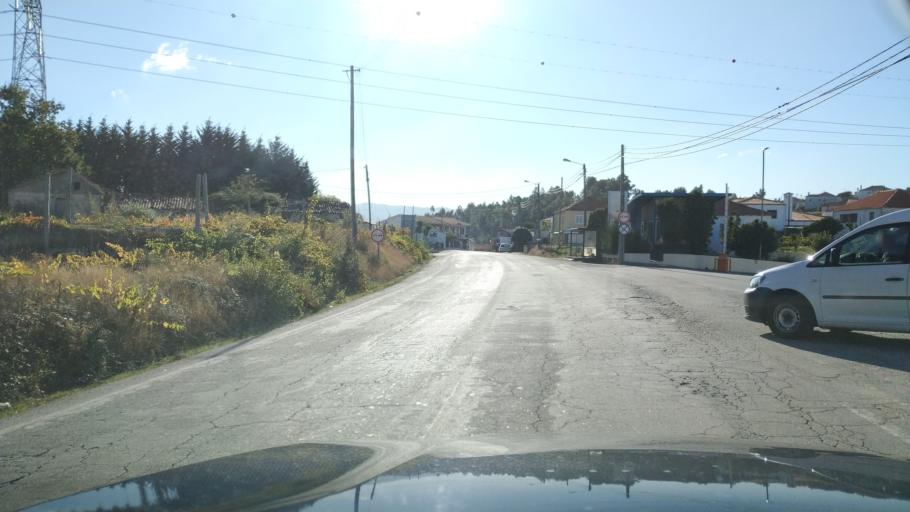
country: PT
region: Aveiro
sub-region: Vale de Cambra
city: Vale de Cambra
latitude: 40.8741
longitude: -8.4159
